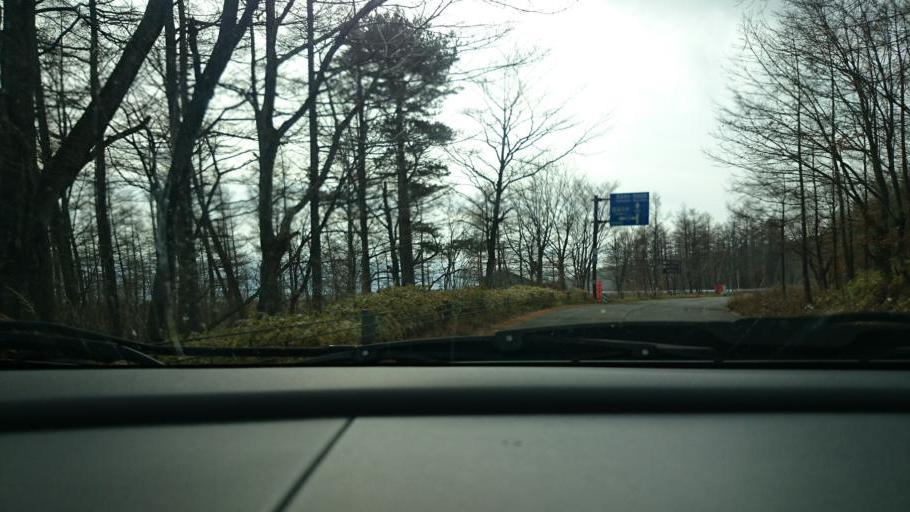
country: JP
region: Tochigi
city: Kuroiso
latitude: 37.1285
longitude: 140.0163
